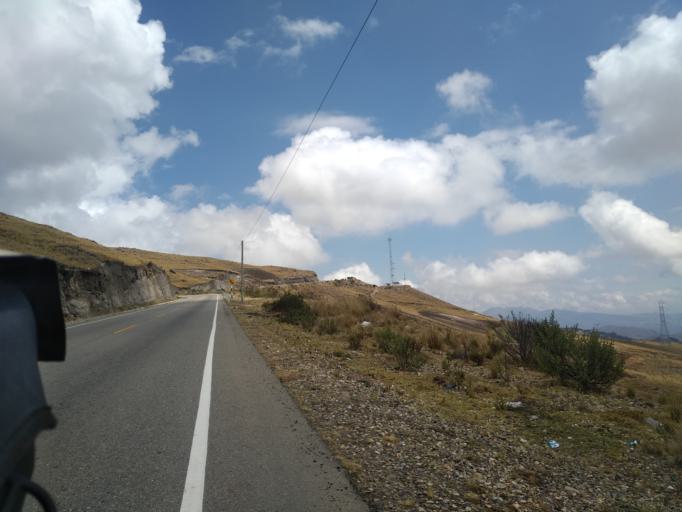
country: PE
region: La Libertad
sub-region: Provincia de Santiago de Chuco
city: Quiruvilca
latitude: -7.9202
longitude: -78.1565
